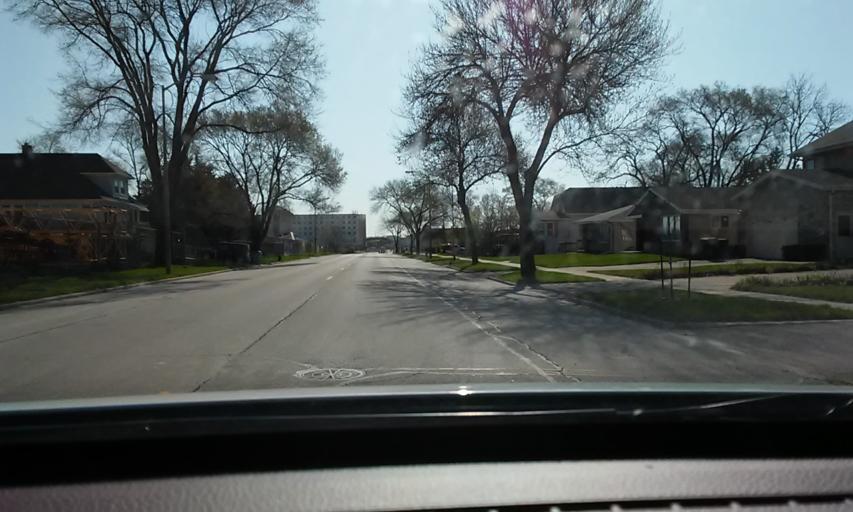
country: US
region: Wisconsin
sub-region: Milwaukee County
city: West Allis
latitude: 43.0239
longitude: -88.0207
